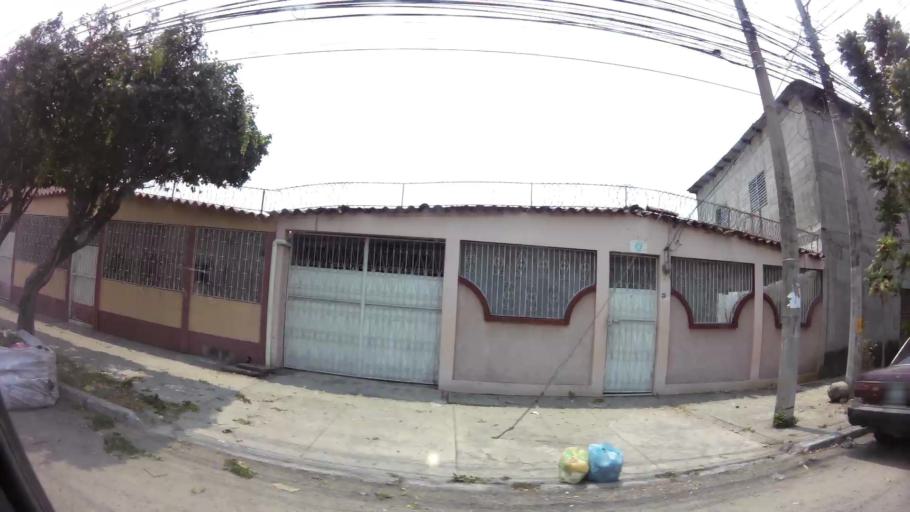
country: HN
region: Cortes
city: San Pedro Sula
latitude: 15.4977
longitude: -88.0100
